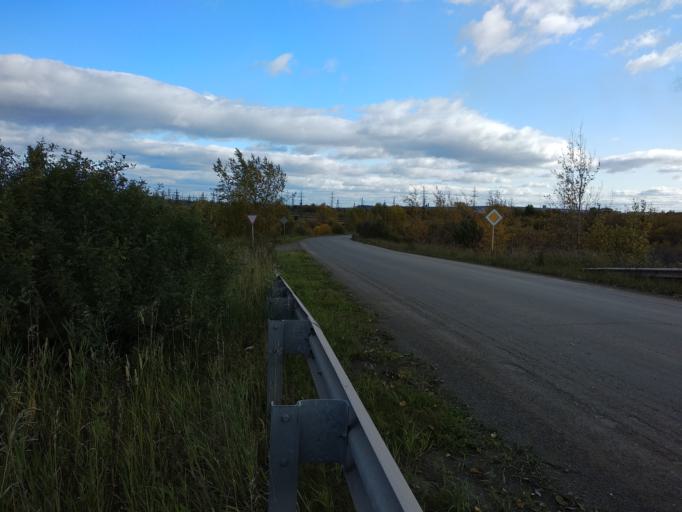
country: RU
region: Sverdlovsk
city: Krasnotur'insk
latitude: 59.7899
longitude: 60.1985
